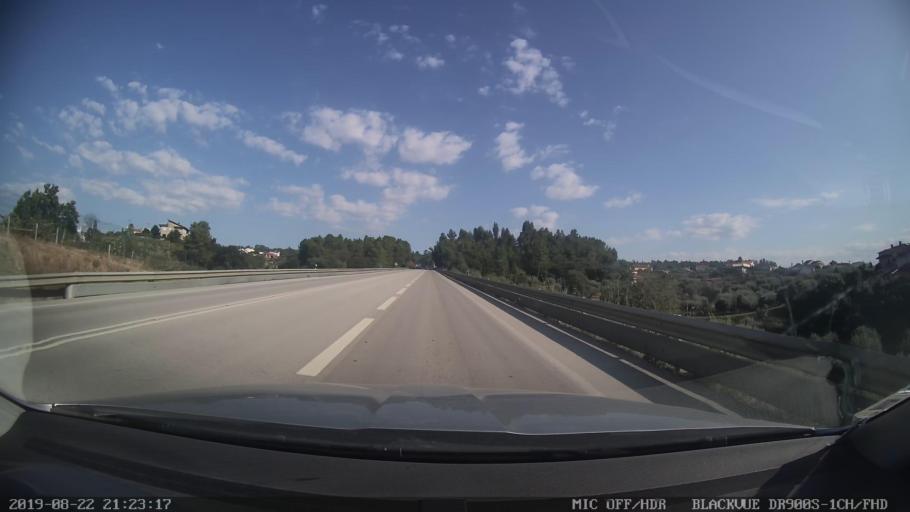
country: PT
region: Castelo Branco
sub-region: Serta
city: Serta
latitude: 39.8287
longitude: -8.1083
